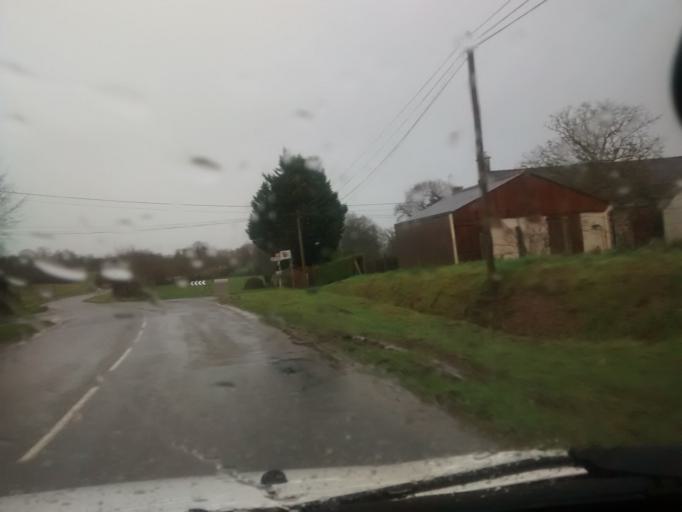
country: FR
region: Brittany
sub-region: Departement d'Ille-et-Vilaine
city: Saint-Pere
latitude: 48.5714
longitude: -1.9054
